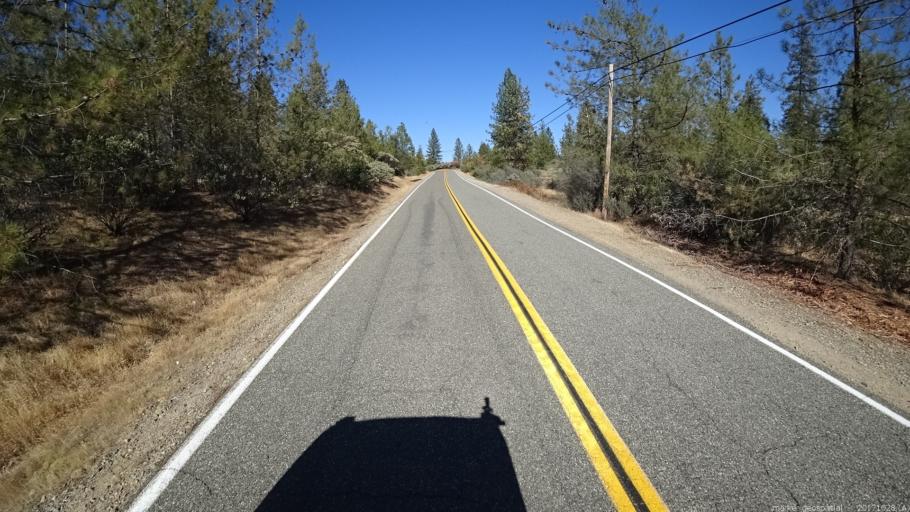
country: US
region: California
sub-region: Shasta County
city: Shasta
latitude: 40.6384
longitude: -122.4562
